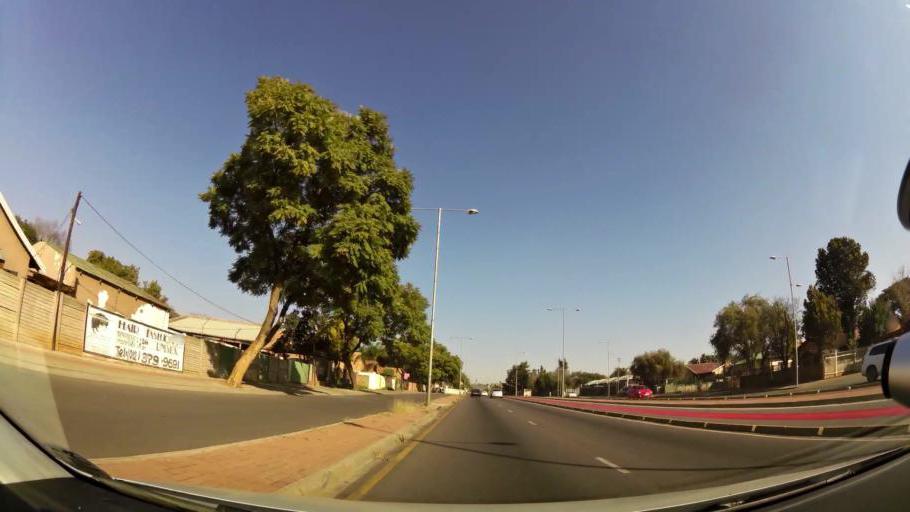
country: ZA
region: Gauteng
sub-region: City of Tshwane Metropolitan Municipality
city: Pretoria
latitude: -25.7035
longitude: 28.1873
